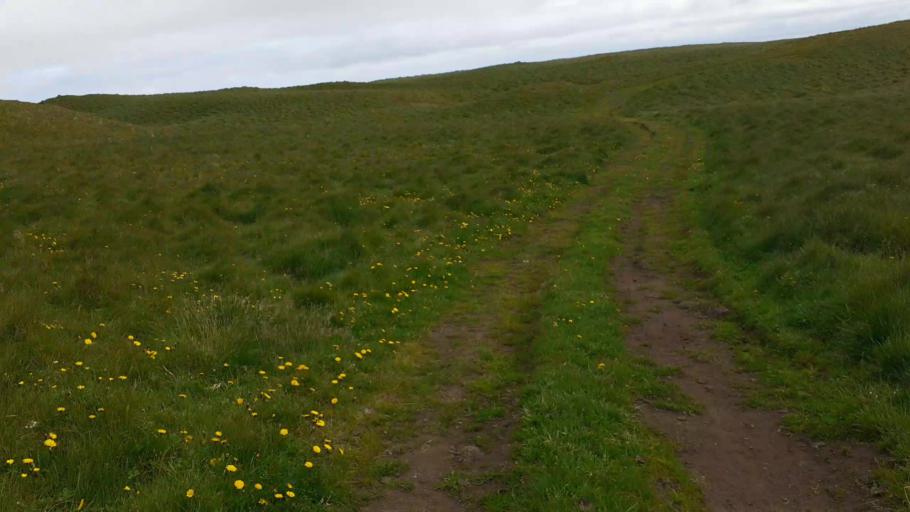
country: IS
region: Northeast
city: Dalvik
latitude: 66.5434
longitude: -17.9853
